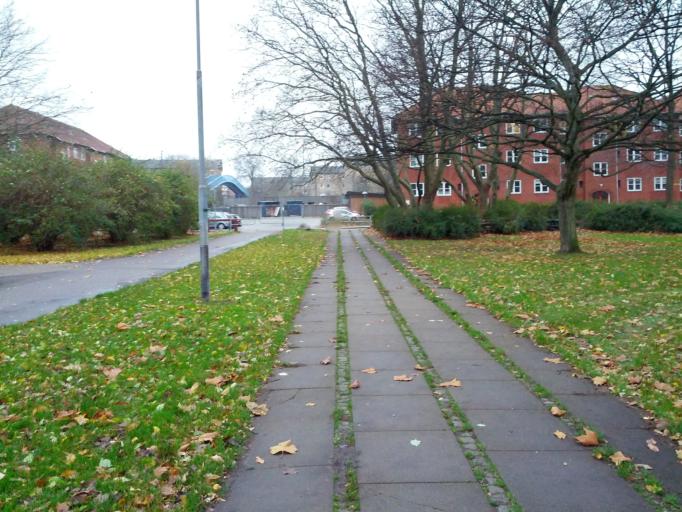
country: DK
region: Capital Region
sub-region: Herlev Kommune
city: Herlev
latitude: 55.7264
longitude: 12.4443
